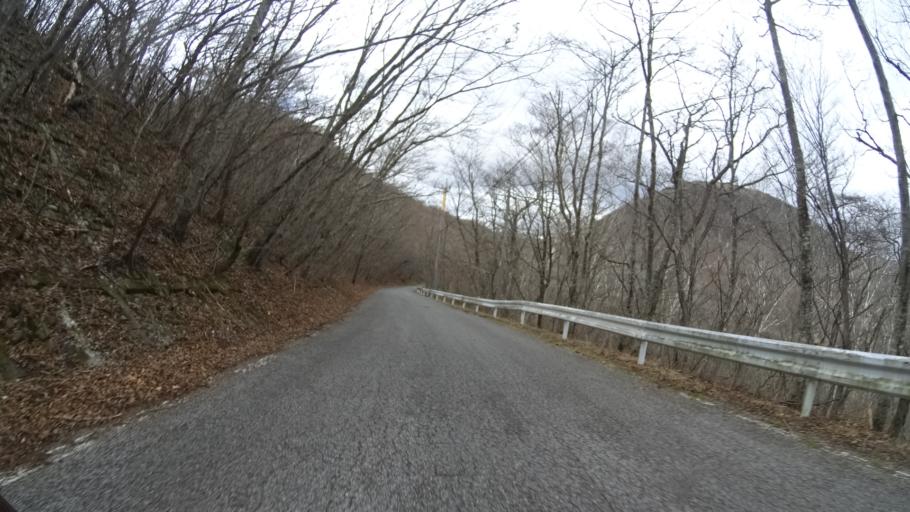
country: JP
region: Gunma
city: Omamacho-omama
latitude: 36.5275
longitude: 139.1726
